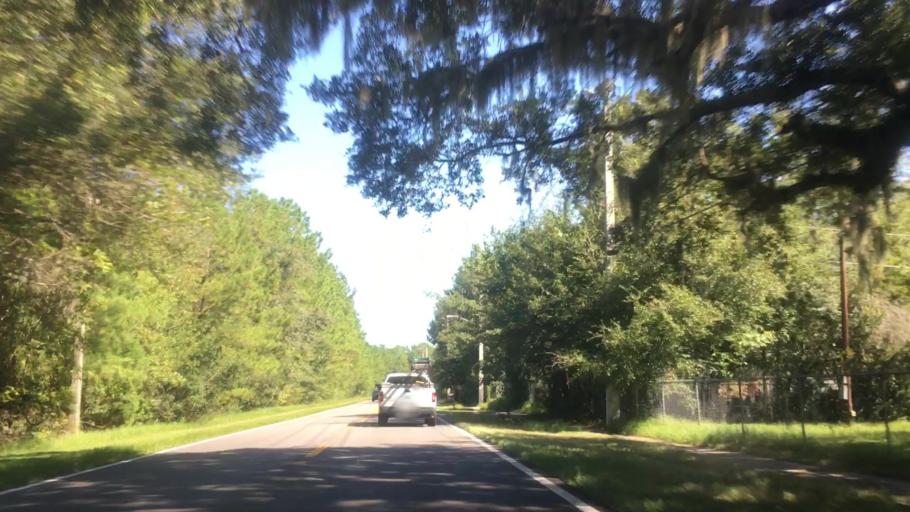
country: US
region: Florida
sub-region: Nassau County
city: Yulee
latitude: 30.4964
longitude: -81.5879
